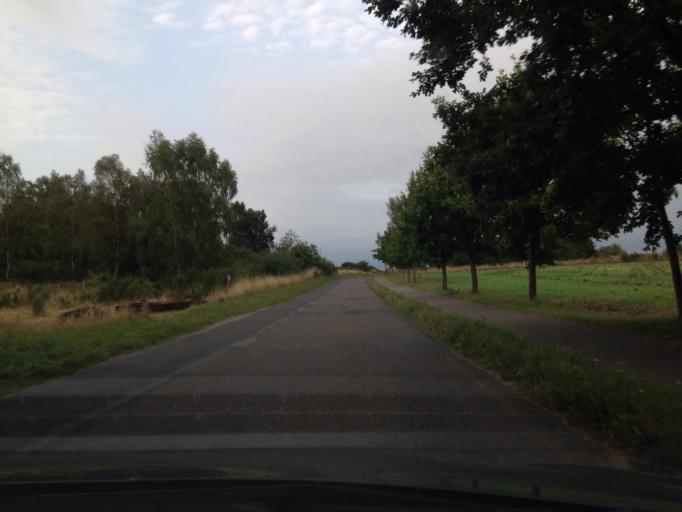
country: DE
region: Mecklenburg-Vorpommern
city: Loitz
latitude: 53.3247
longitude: 13.4162
